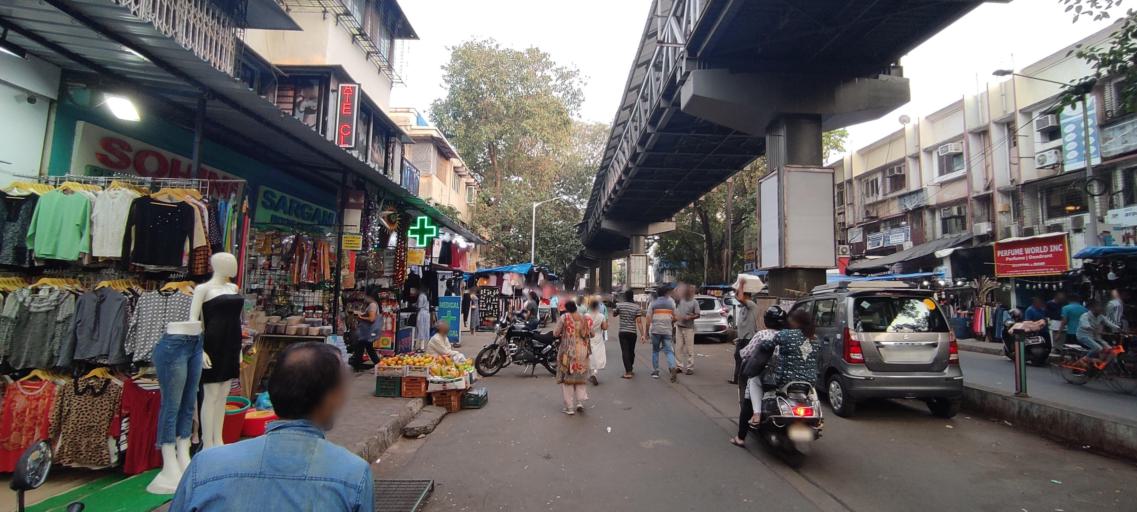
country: IN
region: Maharashtra
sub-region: Mumbai Suburban
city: Mumbai
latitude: 19.1004
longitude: 72.8419
